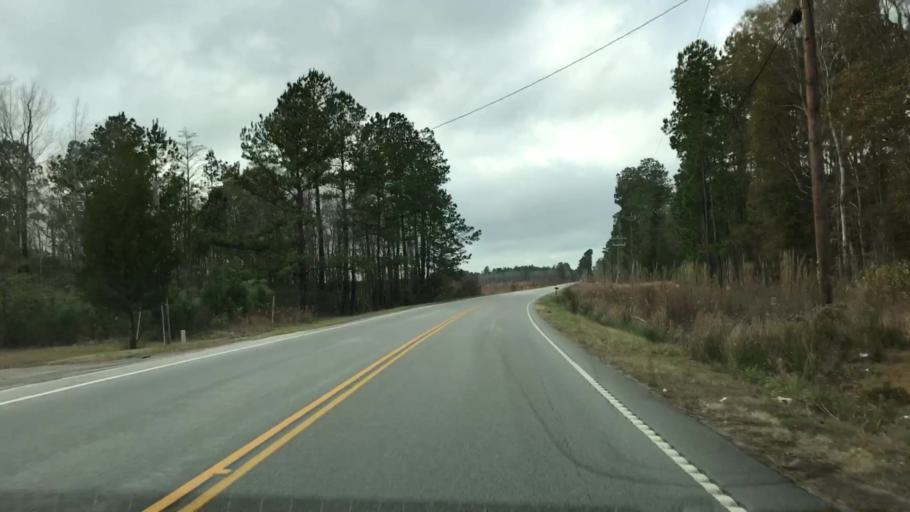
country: US
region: South Carolina
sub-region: Berkeley County
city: Saint Stephen
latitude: 33.2816
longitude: -79.7317
